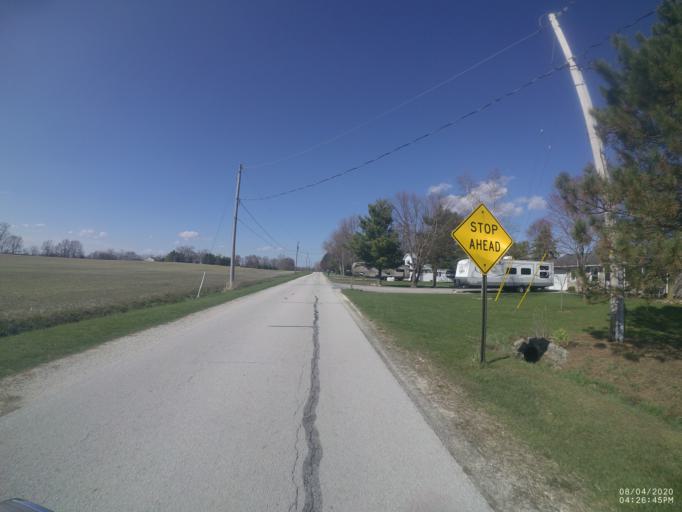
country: US
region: Ohio
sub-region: Sandusky County
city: Stony Prairie
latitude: 41.3238
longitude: -83.2059
